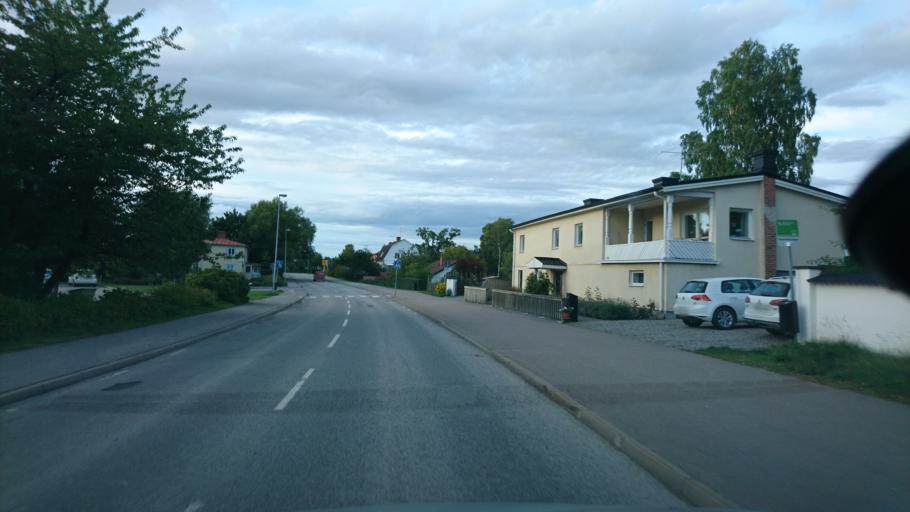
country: SE
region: Soedermanland
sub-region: Strangnas Kommun
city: Stallarholmen
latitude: 59.3606
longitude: 17.2062
